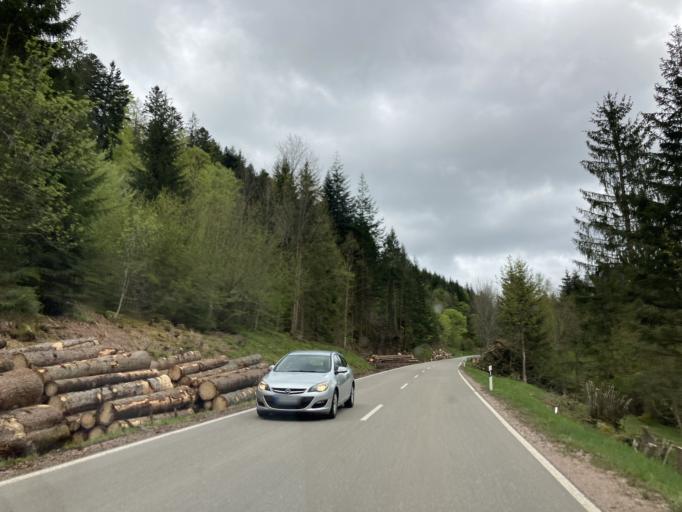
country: DE
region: Baden-Wuerttemberg
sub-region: Freiburg Region
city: Schonach im Schwarzwald
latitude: 48.1383
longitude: 8.1591
